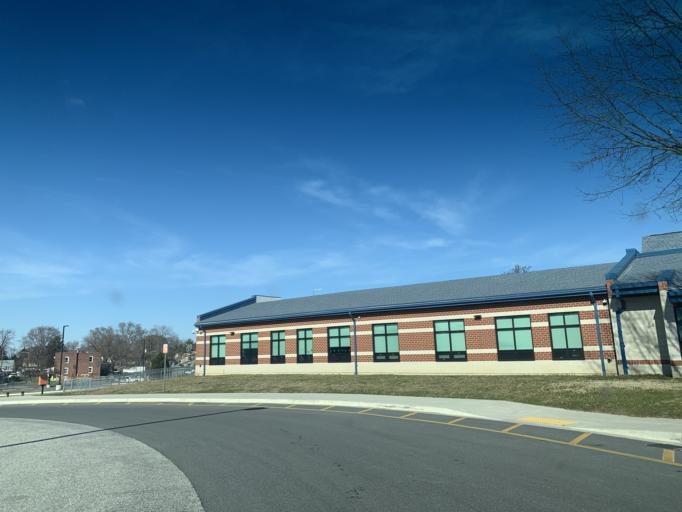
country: US
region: Maryland
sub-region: Anne Arundel County
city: Brooklyn Park
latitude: 39.2230
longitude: -76.6107
